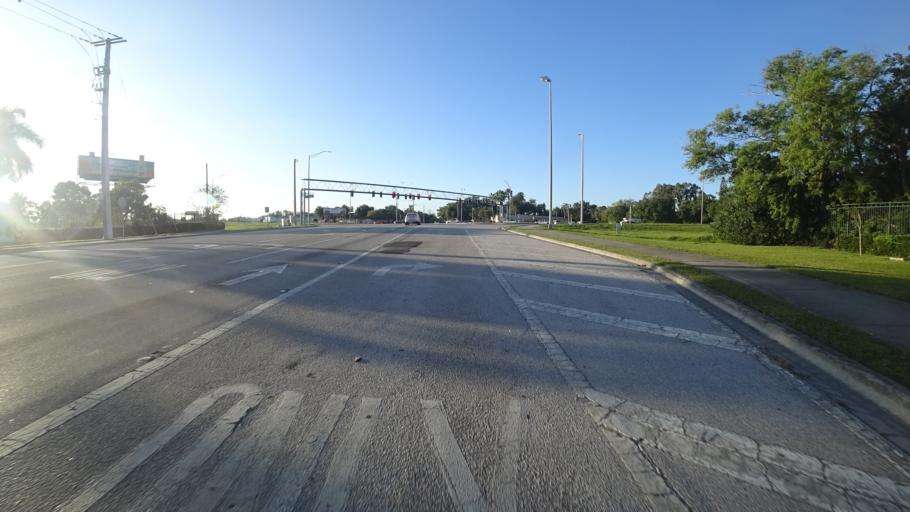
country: US
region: Florida
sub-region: Manatee County
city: West Samoset
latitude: 27.4806
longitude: -82.5548
